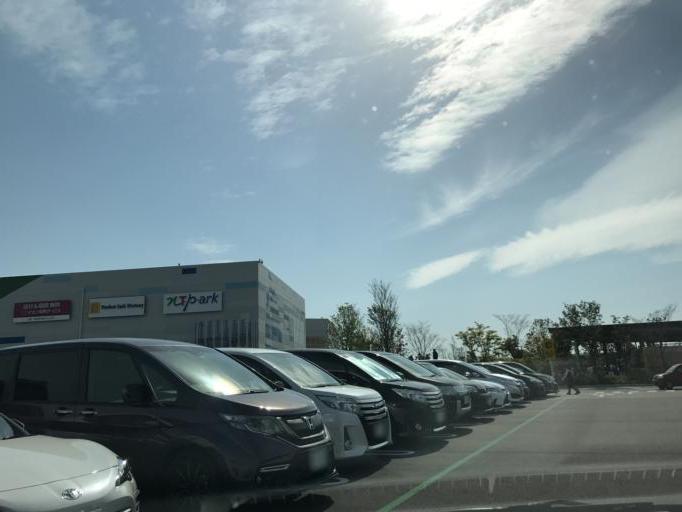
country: JP
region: Aichi
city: Tokoname
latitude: 34.8851
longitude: 136.8266
